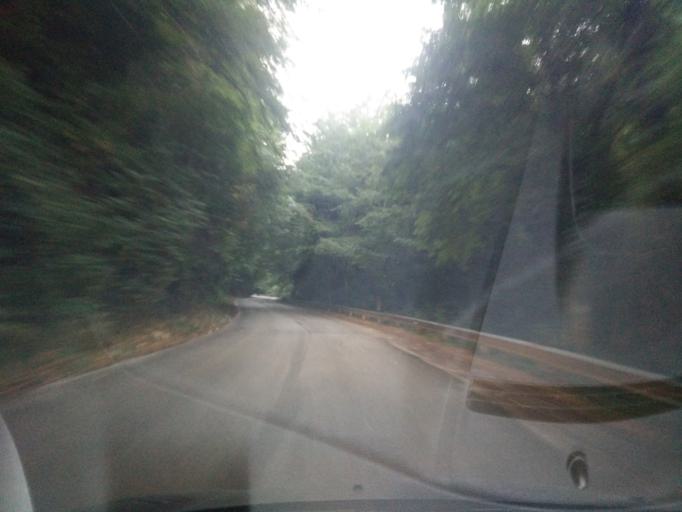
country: IT
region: Apulia
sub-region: Provincia di Foggia
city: Vico del Gargano
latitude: 41.8360
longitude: 16.0406
